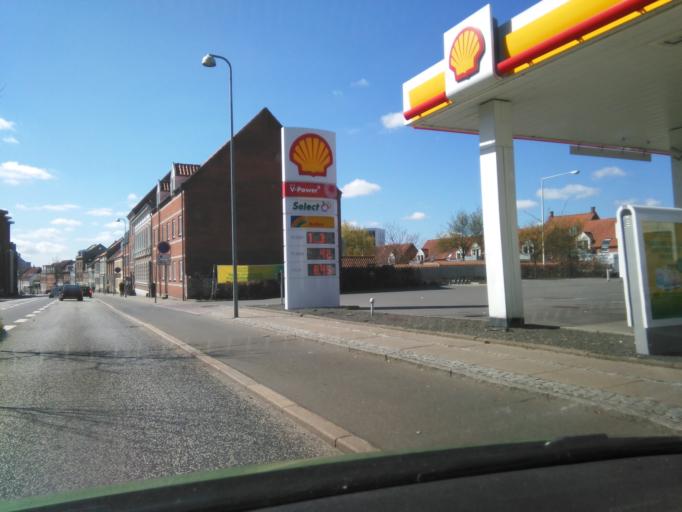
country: DK
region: Central Jutland
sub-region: Horsens Kommune
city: Horsens
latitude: 55.8673
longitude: 9.8447
